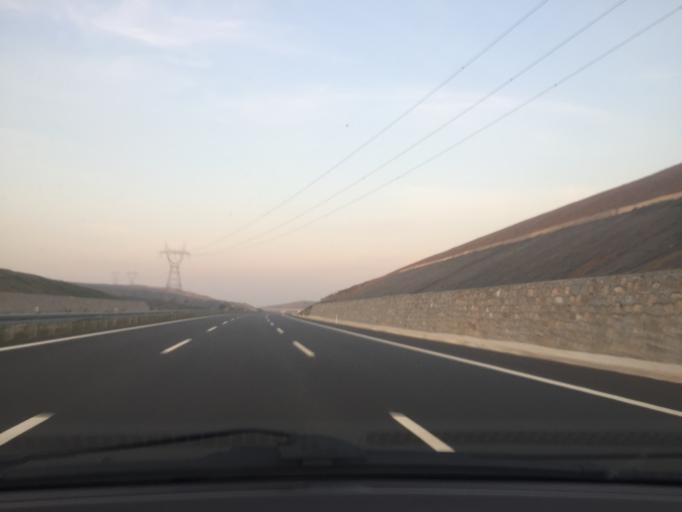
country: TR
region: Bursa
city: Mahmudiye
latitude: 40.2747
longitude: 28.5523
